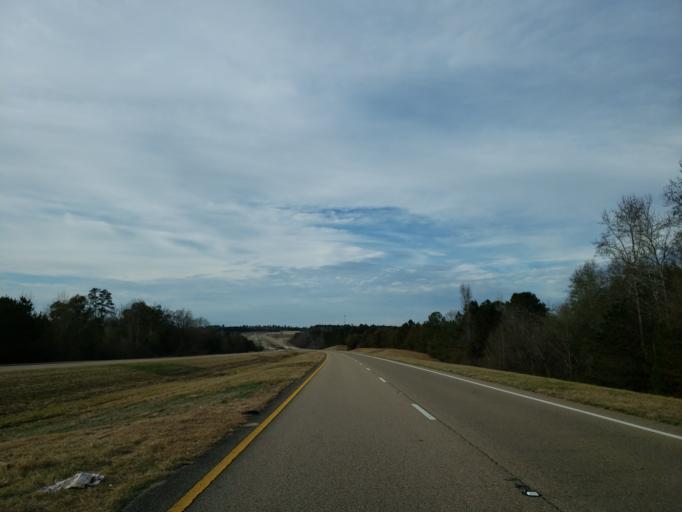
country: US
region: Mississippi
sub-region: Wayne County
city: Waynesboro
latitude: 31.6702
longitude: -88.6063
